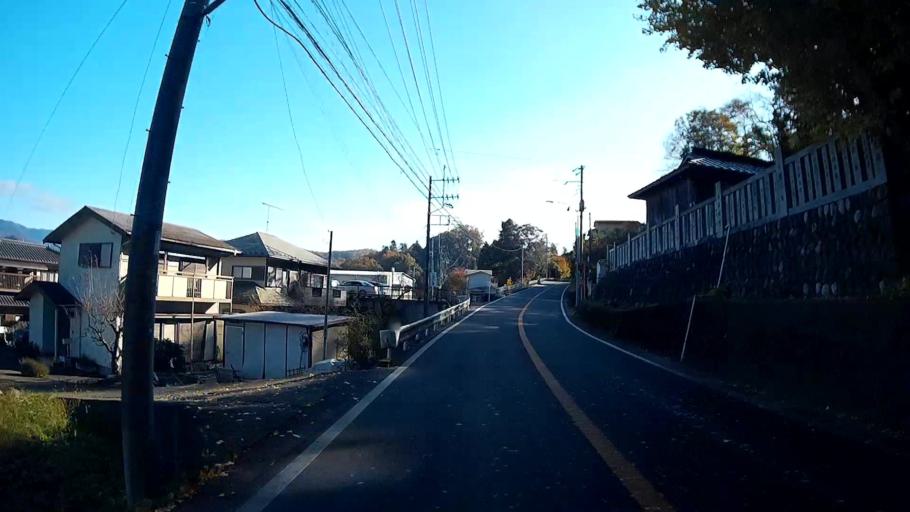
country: JP
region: Yamanashi
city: Uenohara
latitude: 35.6091
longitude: 139.1227
